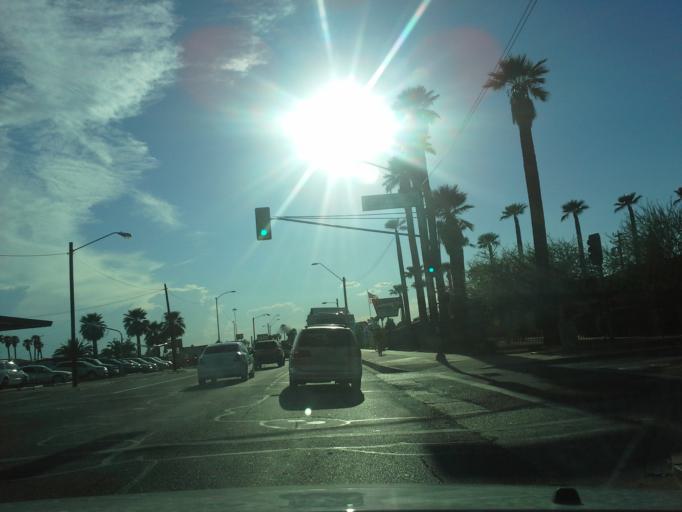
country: US
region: Arizona
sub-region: Maricopa County
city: Phoenix
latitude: 33.4513
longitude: -112.1043
